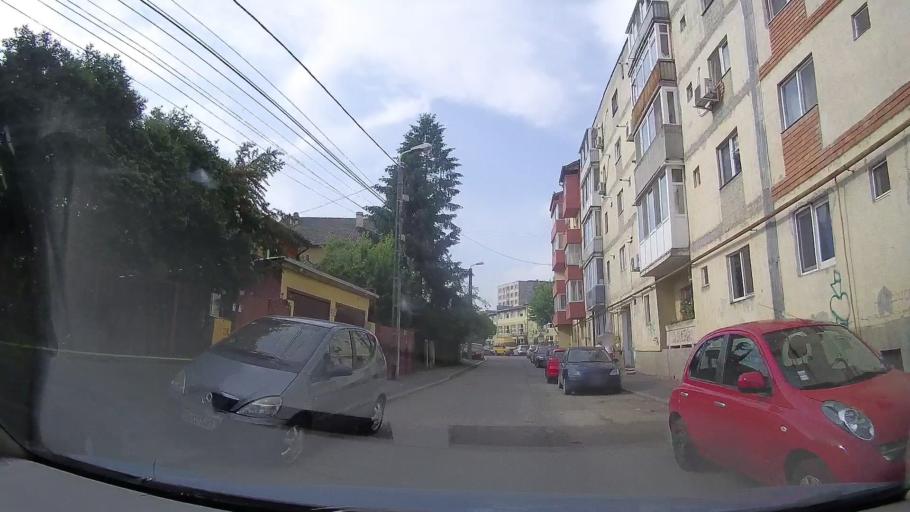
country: RO
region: Timis
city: Timisoara
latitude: 45.7452
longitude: 21.2439
